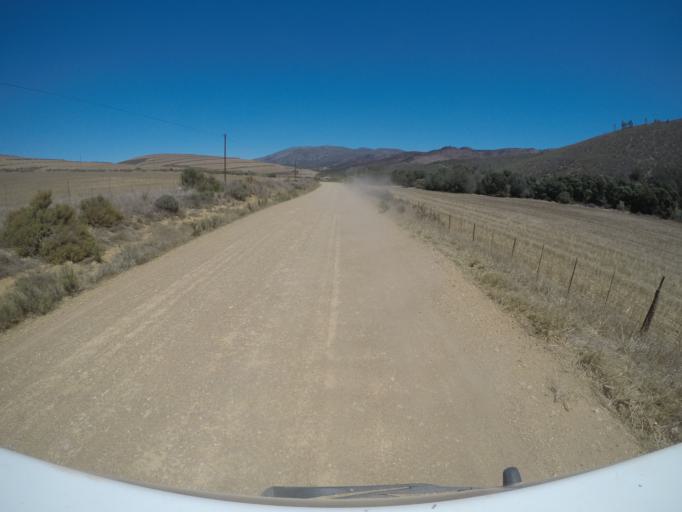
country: ZA
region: Western Cape
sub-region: Overberg District Municipality
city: Caledon
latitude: -34.1487
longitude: 19.2416
